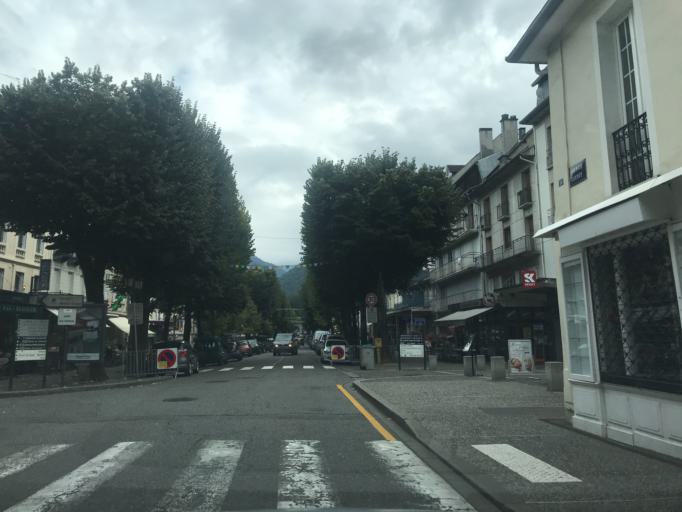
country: FR
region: Midi-Pyrenees
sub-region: Departement de la Haute-Garonne
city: Bagneres-de-Luchon
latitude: 42.7905
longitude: 0.5914
